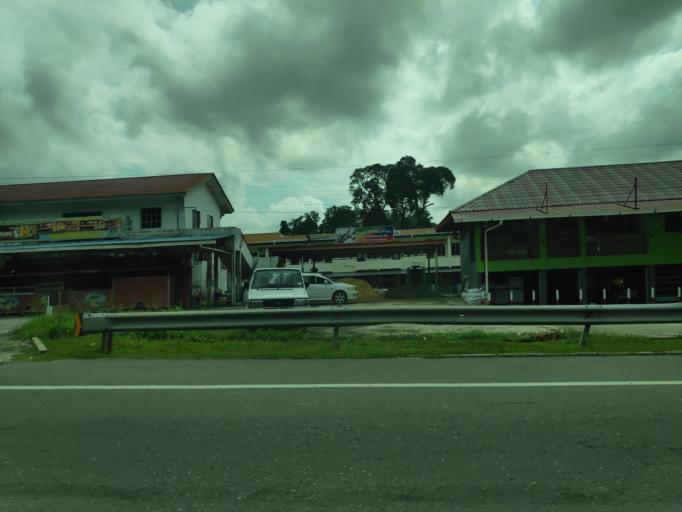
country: BN
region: Brunei and Muara
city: Bandar Seri Begawan
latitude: 4.8797
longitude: 114.8773
